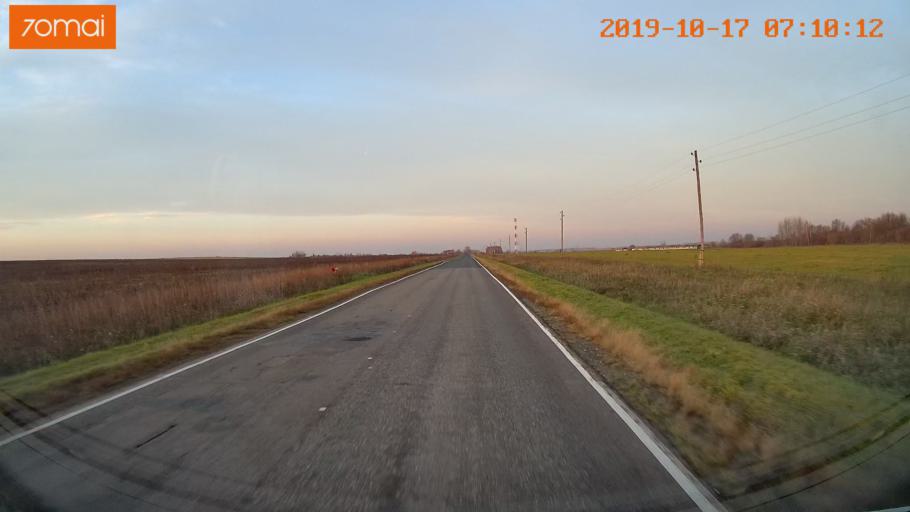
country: RU
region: Vladimir
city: Suzdal'
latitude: 56.4134
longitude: 40.3666
